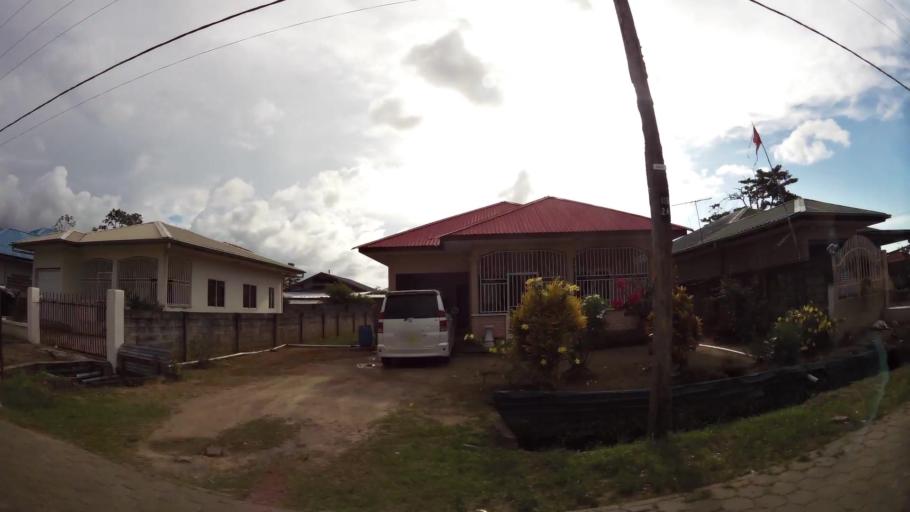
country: SR
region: Paramaribo
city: Paramaribo
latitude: 5.8460
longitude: -55.1781
